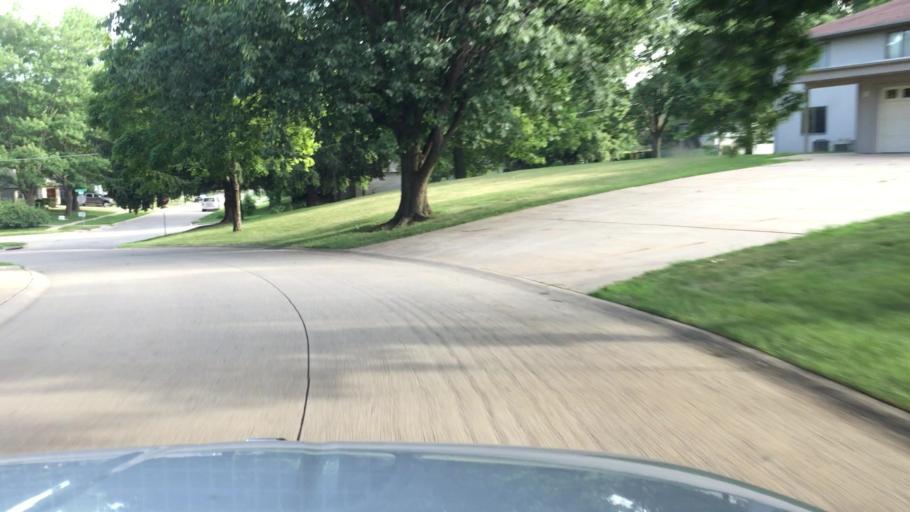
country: US
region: Iowa
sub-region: Johnson County
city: Iowa City
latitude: 41.6612
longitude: -91.4932
